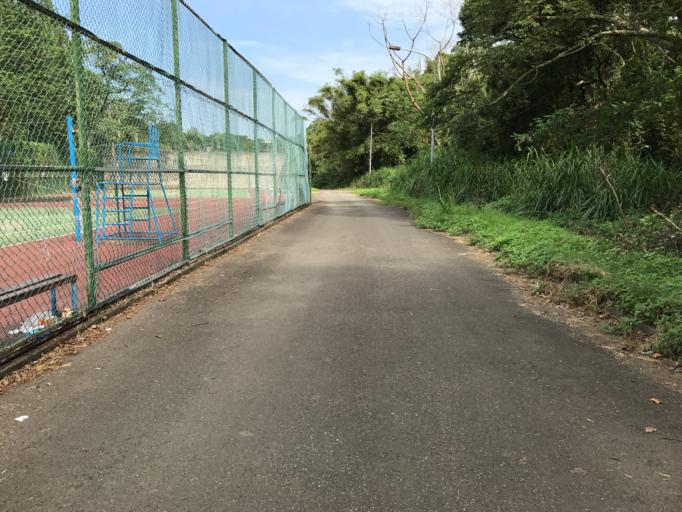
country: TW
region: Taiwan
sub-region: Hsinchu
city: Hsinchu
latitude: 24.7615
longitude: 120.9553
